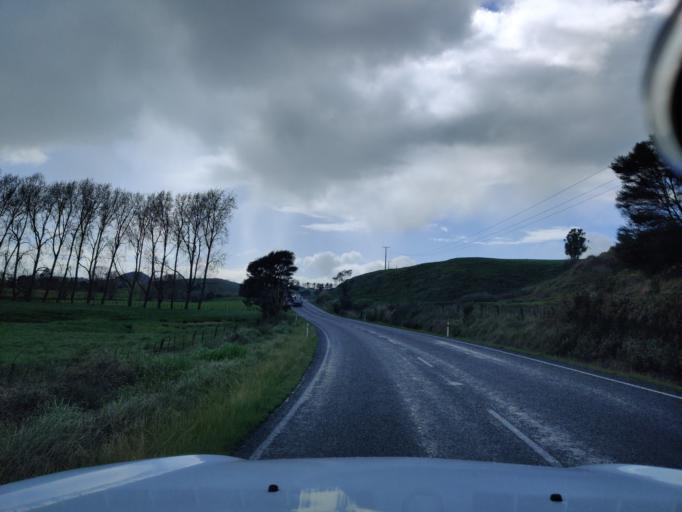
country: NZ
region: Waikato
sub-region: Waikato District
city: Ngaruawahia
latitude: -37.5813
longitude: 175.2193
